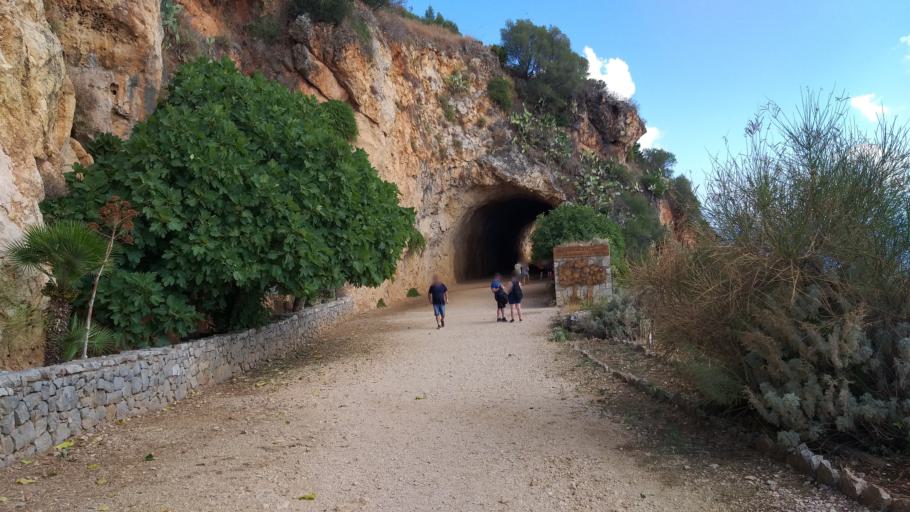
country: IT
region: Sicily
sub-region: Trapani
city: Castelluzzo
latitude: 38.0824
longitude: 12.8075
